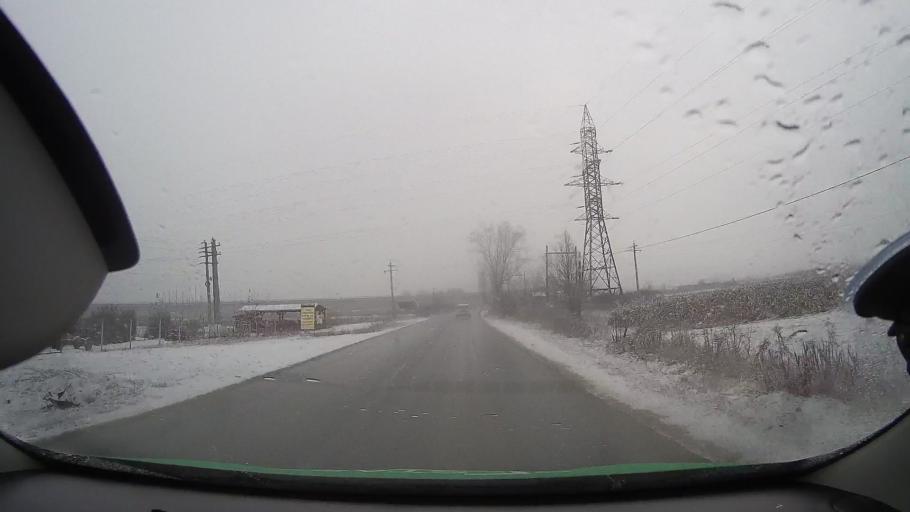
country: RO
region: Alba
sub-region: Municipiul Aiud
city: Sancrai
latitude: 46.3052
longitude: 23.7452
